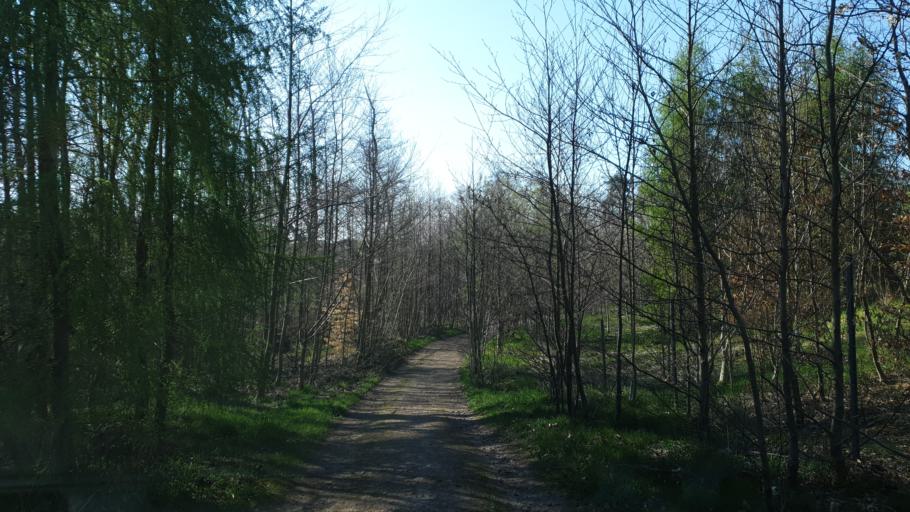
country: DE
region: Saxony
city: Hohndorf
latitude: 50.7386
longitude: 12.6873
